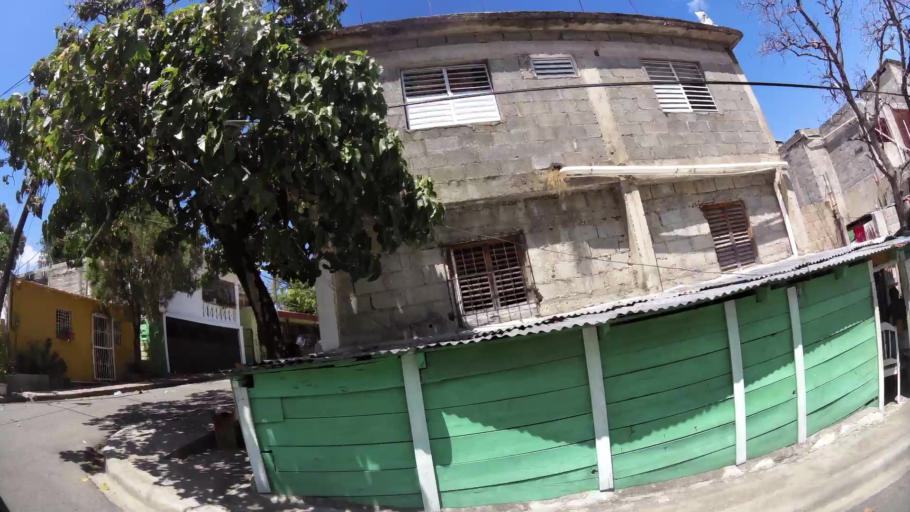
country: DO
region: San Cristobal
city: San Cristobal
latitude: 18.4046
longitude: -70.1140
